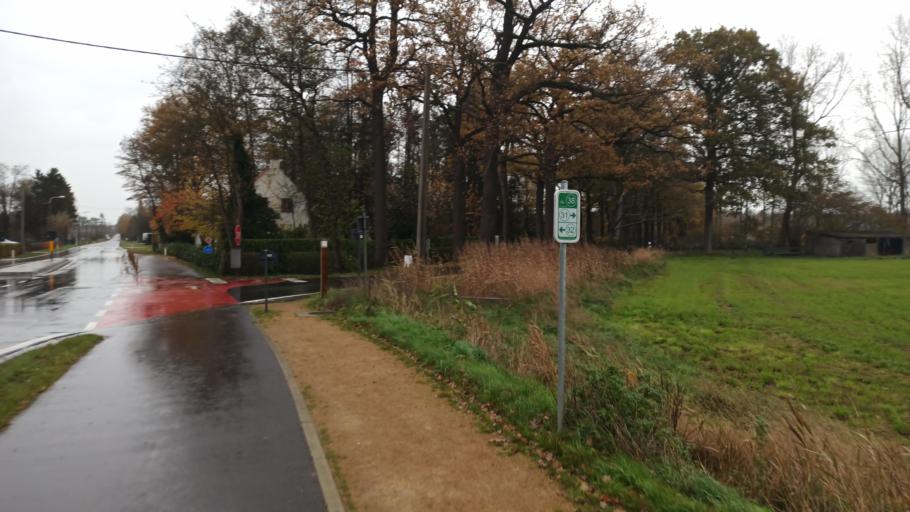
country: BE
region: Flanders
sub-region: Provincie West-Vlaanderen
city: Wingene
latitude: 51.0903
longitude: 3.3093
